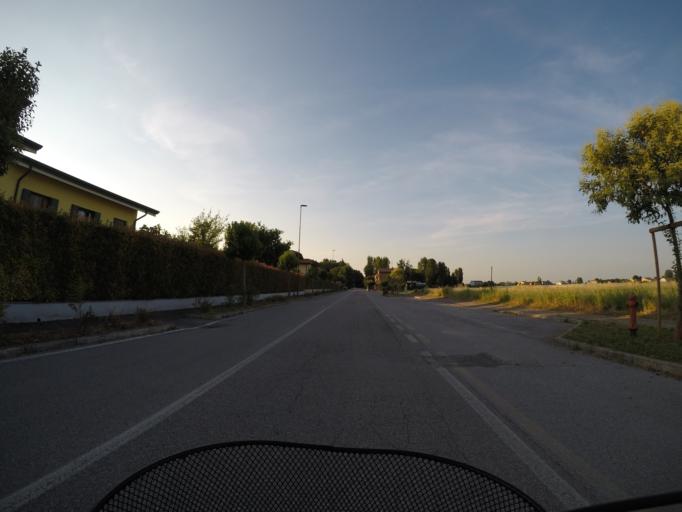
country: IT
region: Veneto
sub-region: Provincia di Rovigo
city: San Bellino
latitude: 45.0284
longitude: 11.5940
